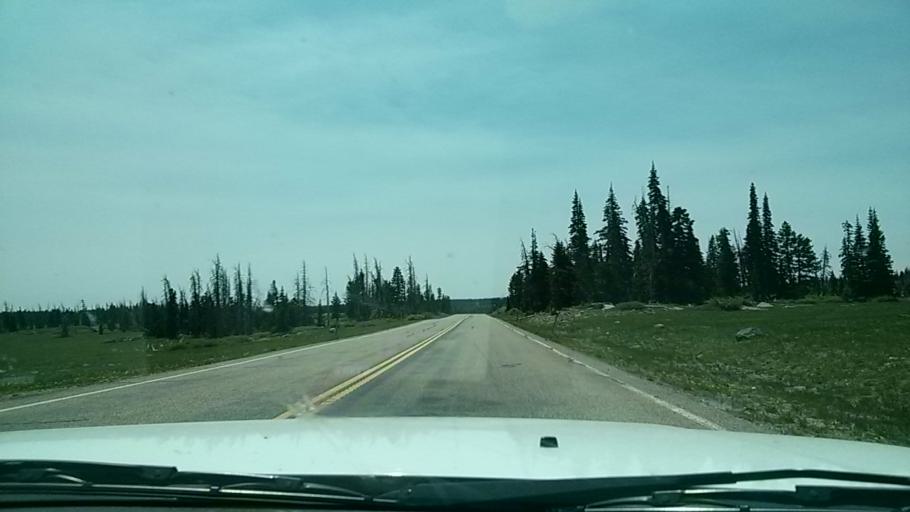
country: US
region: Utah
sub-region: Iron County
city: Cedar City
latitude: 37.6003
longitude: -112.8503
